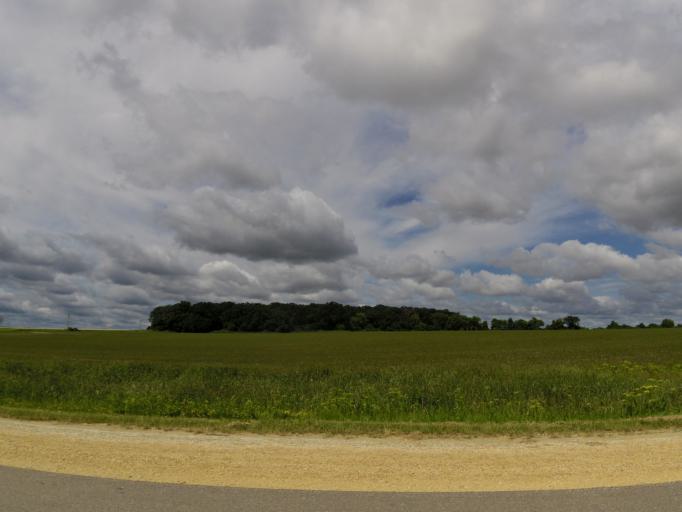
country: US
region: Minnesota
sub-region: Mower County
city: Grand Meadow
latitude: 43.7123
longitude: -92.4794
